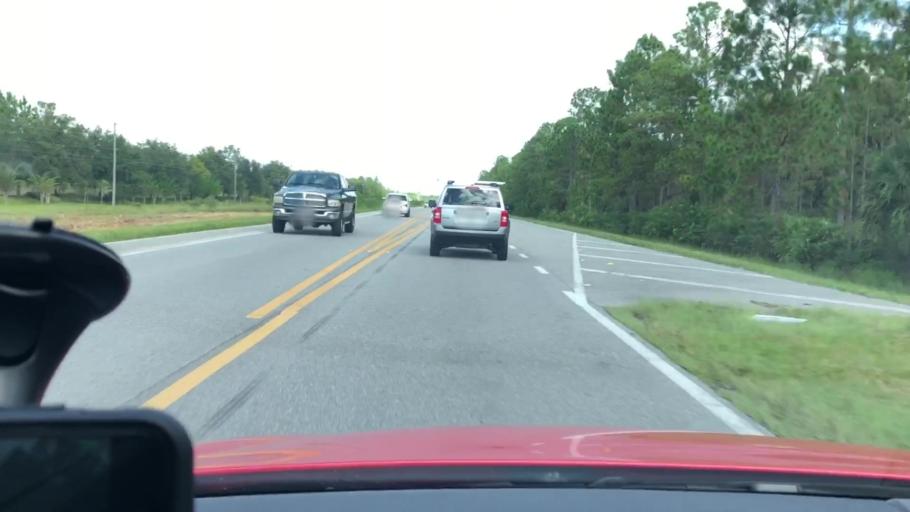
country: US
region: Florida
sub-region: Volusia County
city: Holly Hill
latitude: 29.1978
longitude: -81.1198
